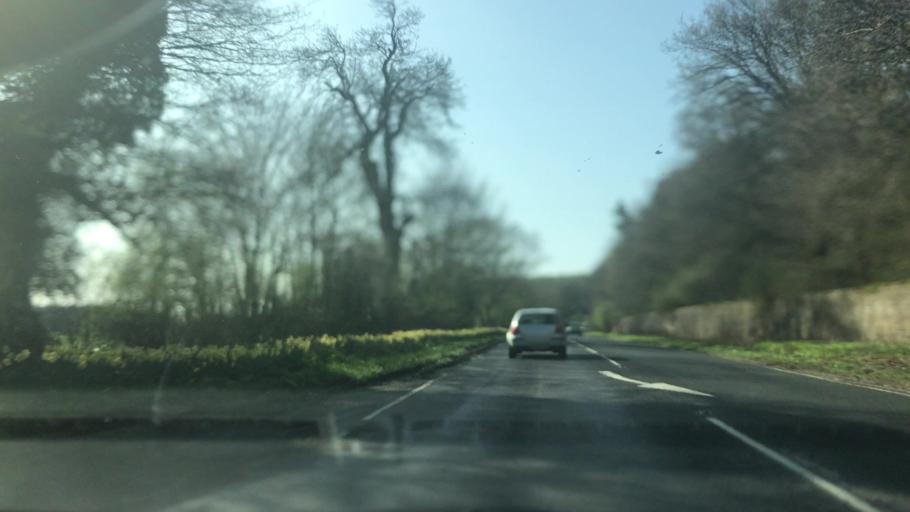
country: GB
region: England
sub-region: City and Borough of Leeds
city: Shadwell
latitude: 53.8875
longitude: -1.5084
